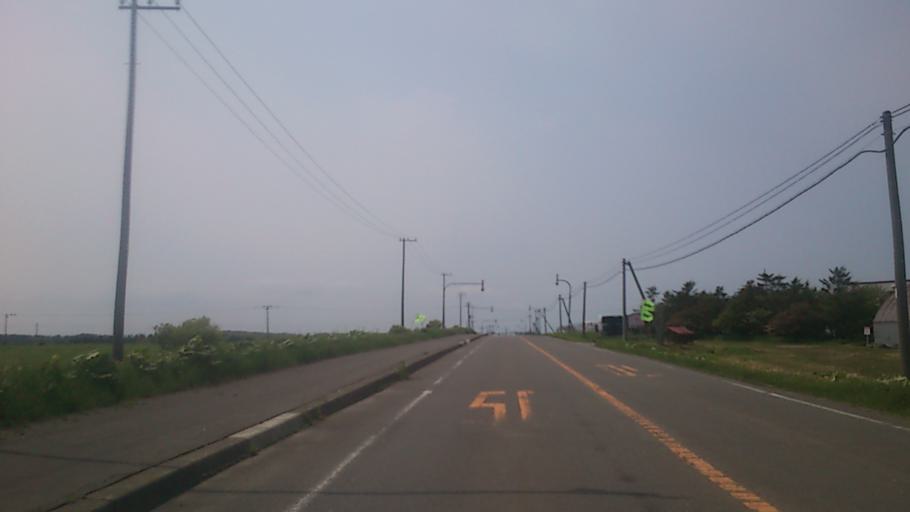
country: JP
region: Hokkaido
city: Nemuro
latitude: 43.2730
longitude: 145.5325
